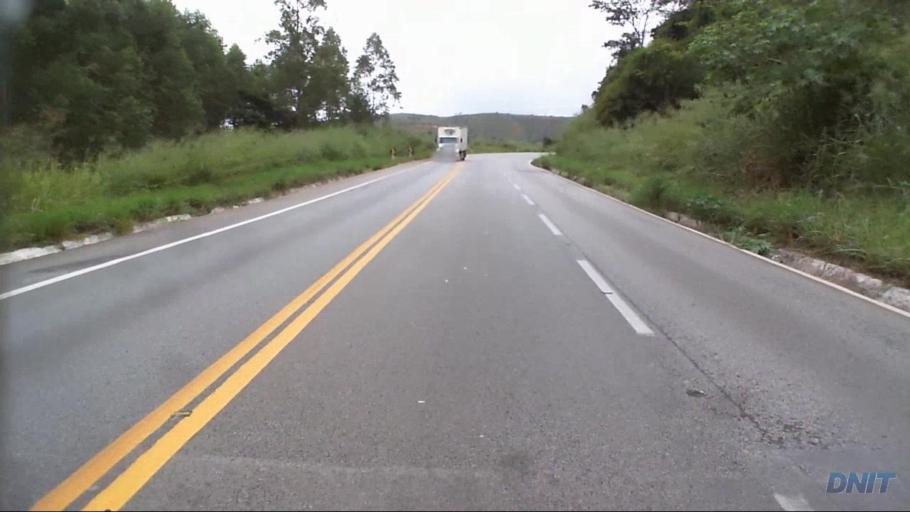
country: BR
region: Minas Gerais
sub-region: Nova Era
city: Nova Era
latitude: -19.7861
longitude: -43.0454
